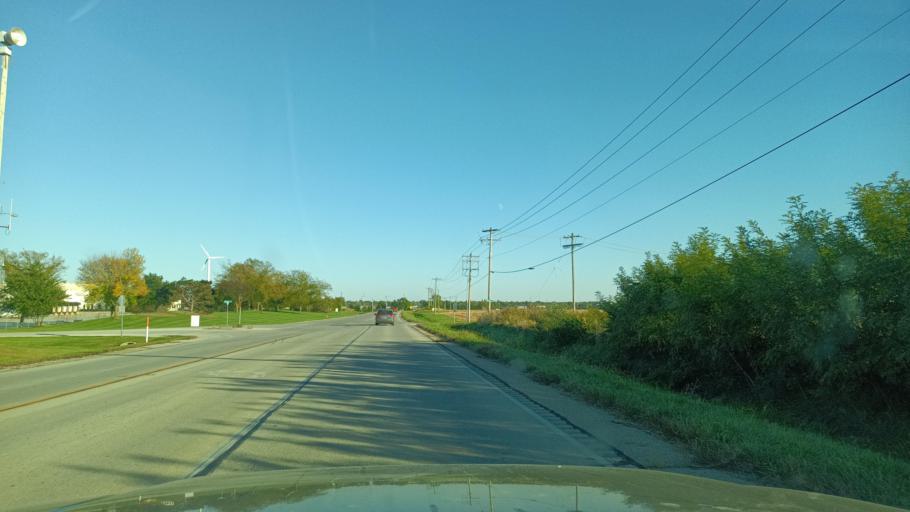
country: US
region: Illinois
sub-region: Champaign County
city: Champaign
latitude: 40.1516
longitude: -88.2968
